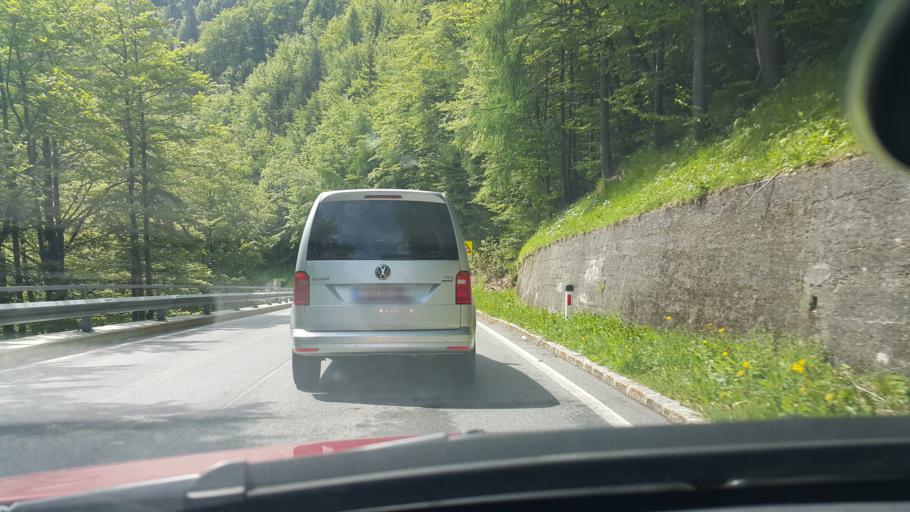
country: AT
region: Carinthia
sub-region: Politischer Bezirk Klagenfurt Land
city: Ferlach
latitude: 46.4476
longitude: 14.2547
